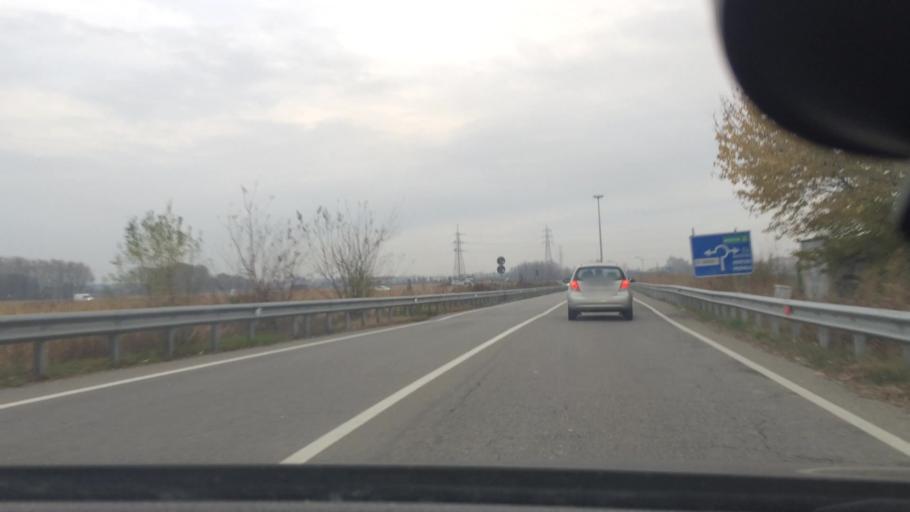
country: IT
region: Lombardy
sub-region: Provincia di Varese
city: Saronno
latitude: 45.6233
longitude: 9.0561
